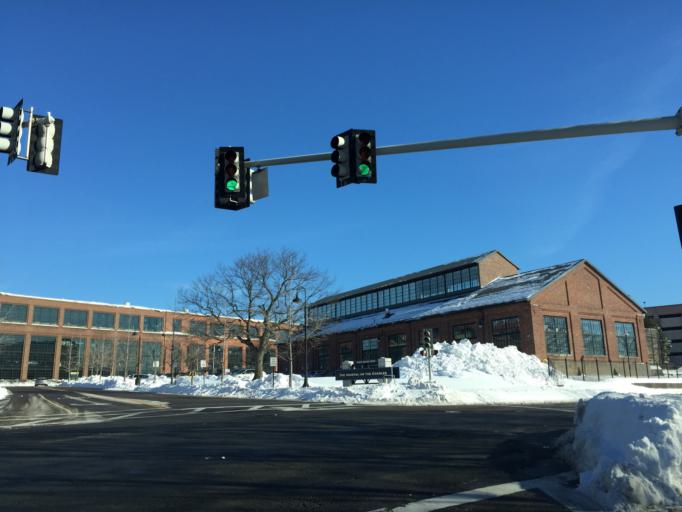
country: US
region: Massachusetts
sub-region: Middlesex County
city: Watertown
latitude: 42.3623
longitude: -71.1682
